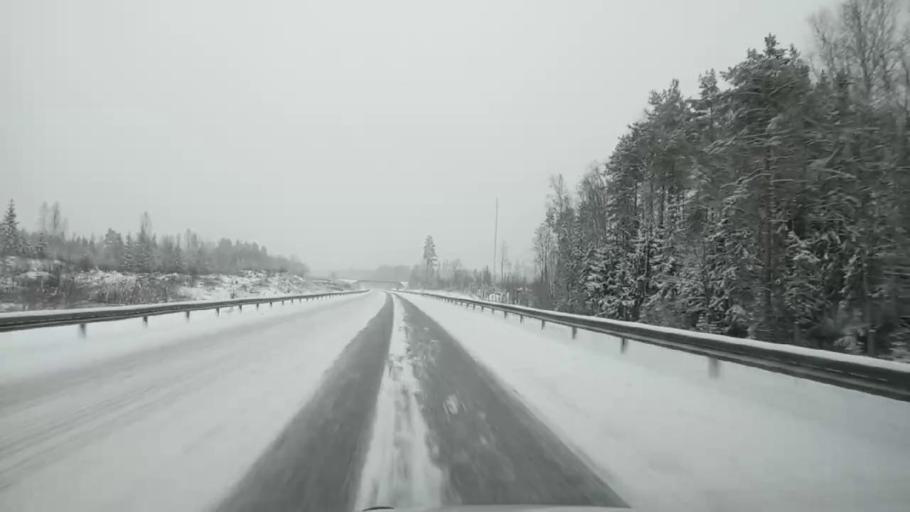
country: SE
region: Uppsala
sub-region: Alvkarleby Kommun
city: AElvkarleby
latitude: 60.5196
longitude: 17.2796
